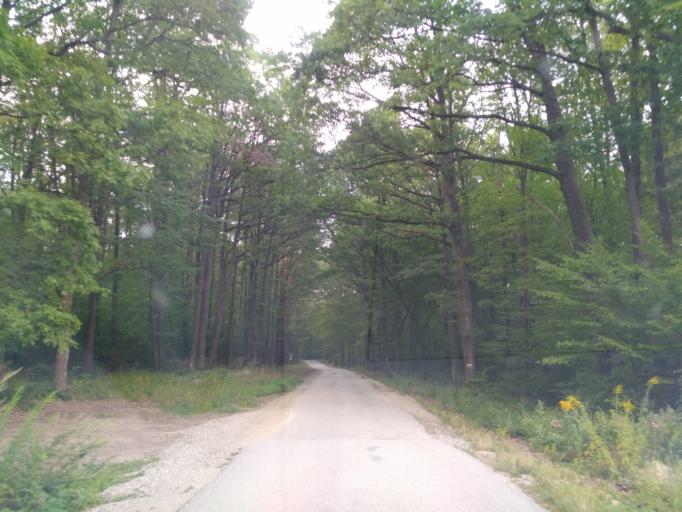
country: SK
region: Kosicky
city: Kosice
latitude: 48.7281
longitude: 21.1824
